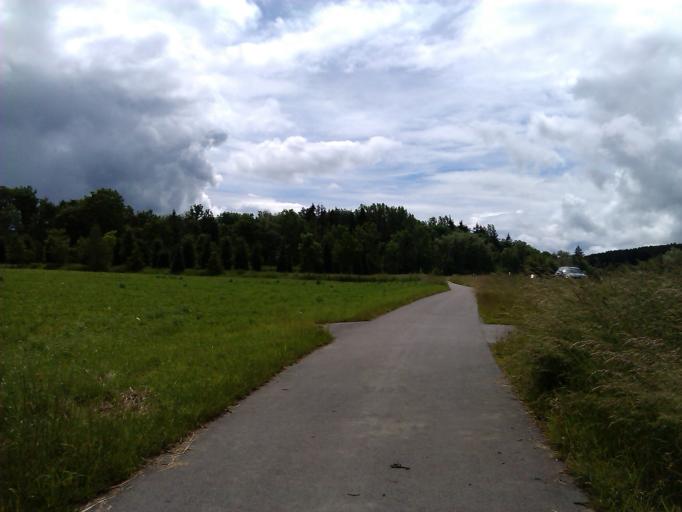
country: DE
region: Bavaria
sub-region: Swabia
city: Pforzen
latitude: 47.9091
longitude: 10.6074
